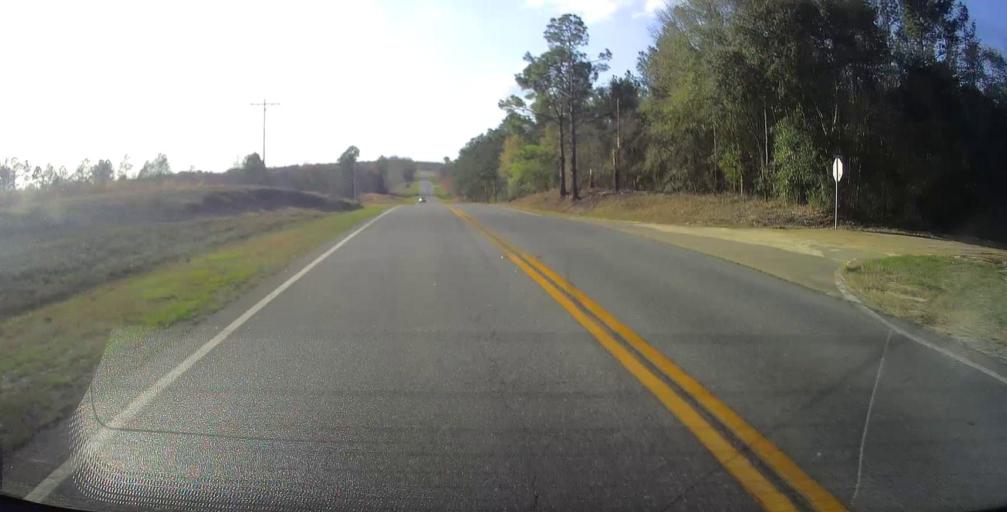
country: US
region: Georgia
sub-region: Tattnall County
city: Reidsville
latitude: 32.1296
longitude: -82.2155
